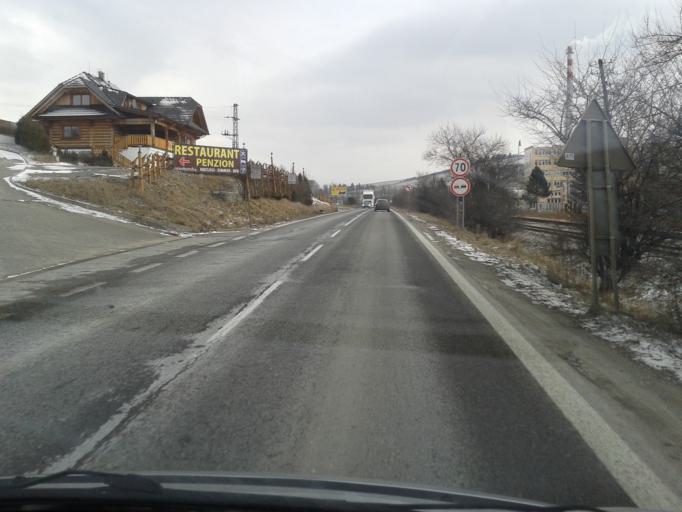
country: SK
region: Zilinsky
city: Tvrdosin
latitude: 49.3111
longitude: 19.5304
